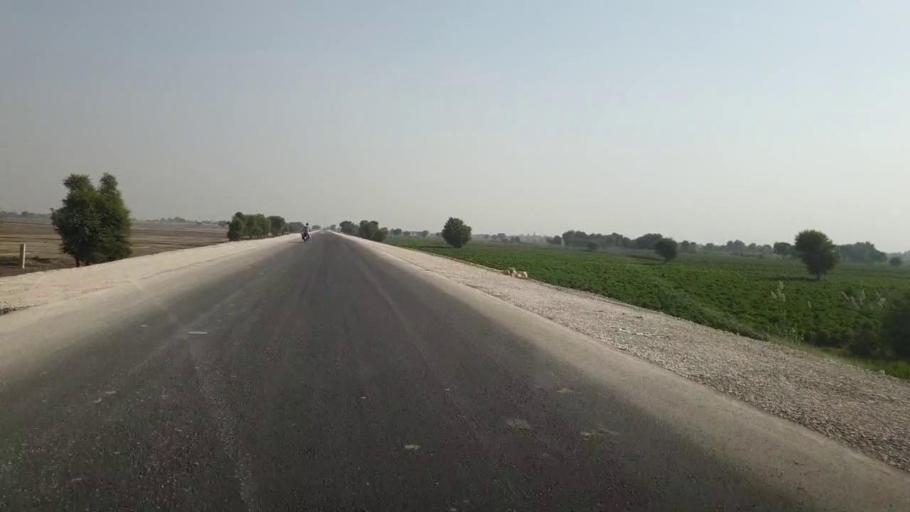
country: PK
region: Sindh
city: Bhan
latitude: 26.5599
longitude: 67.7748
